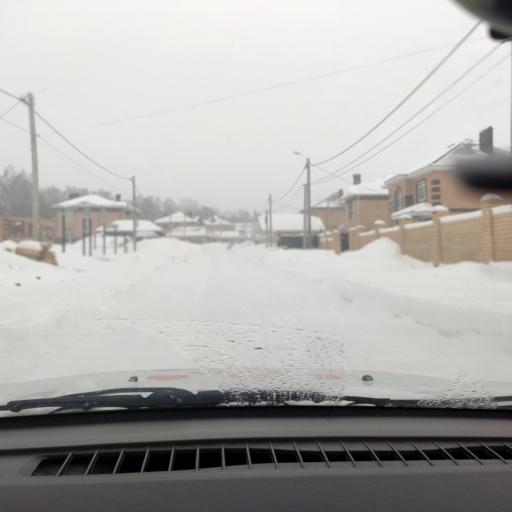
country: RU
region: Bashkortostan
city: Mikhaylovka
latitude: 54.8328
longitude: 55.8749
